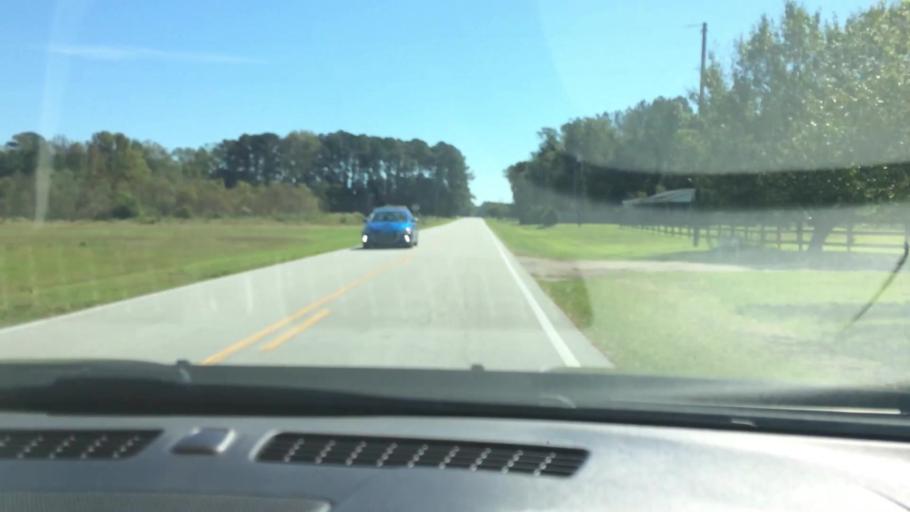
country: US
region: North Carolina
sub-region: Pitt County
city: Grifton
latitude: 35.3417
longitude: -77.3144
